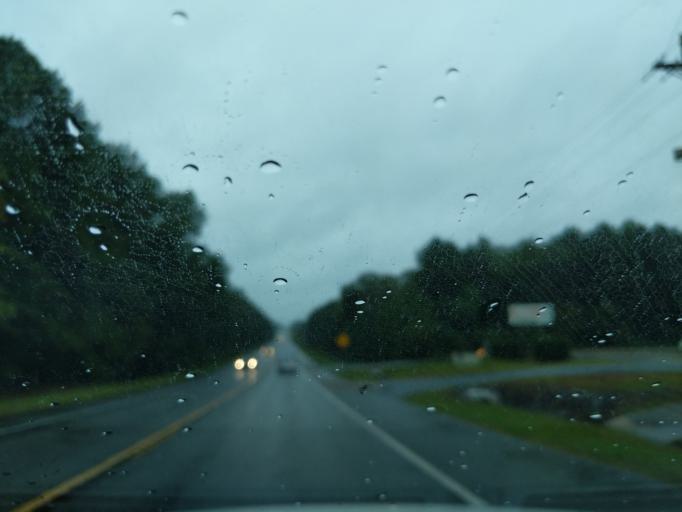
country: US
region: Louisiana
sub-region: Webster Parish
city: Minden
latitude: 32.6232
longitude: -93.2497
